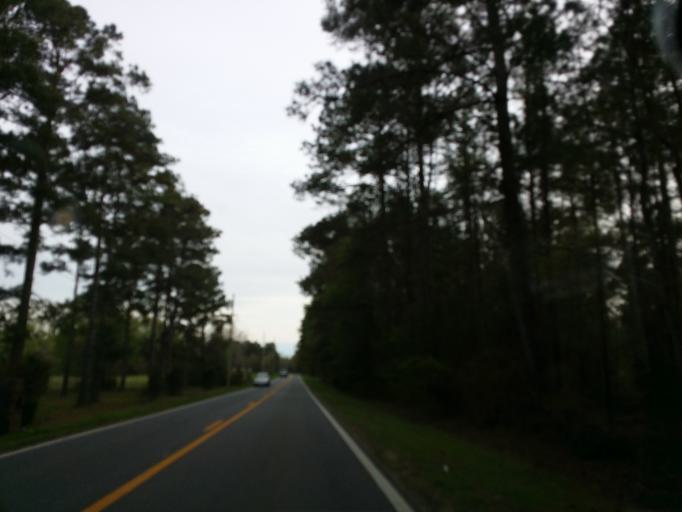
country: US
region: Florida
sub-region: Leon County
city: Tallahassee
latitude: 30.5213
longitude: -84.1299
